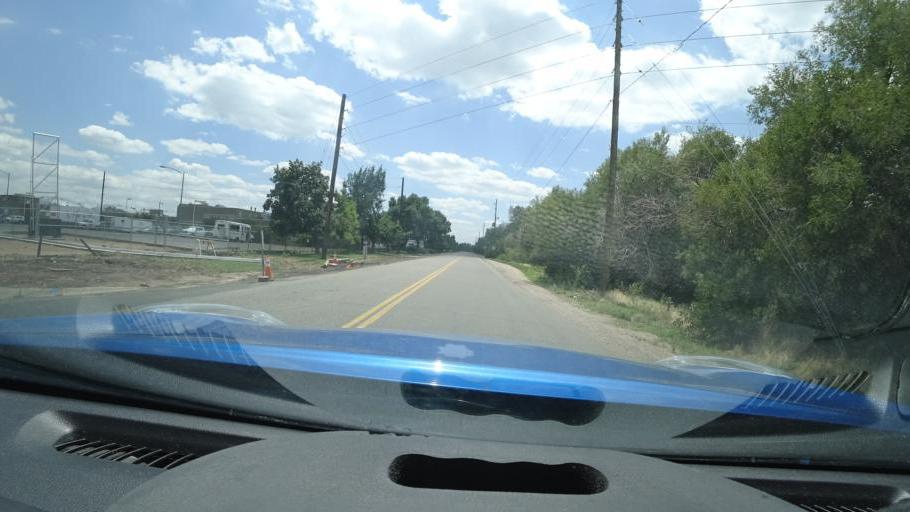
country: US
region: Colorado
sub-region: Arapahoe County
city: Englewood
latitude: 39.6657
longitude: -105.0042
